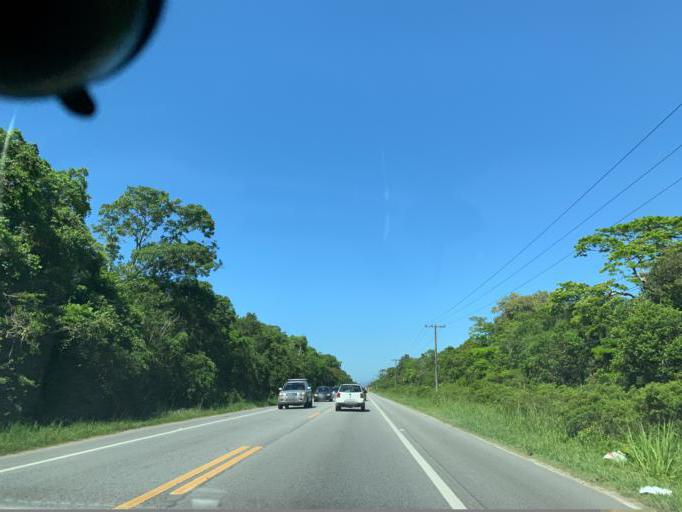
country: BR
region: Sao Paulo
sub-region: Biritiba-Mirim
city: Biritiba Mirim
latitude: -23.7645
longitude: -45.9235
